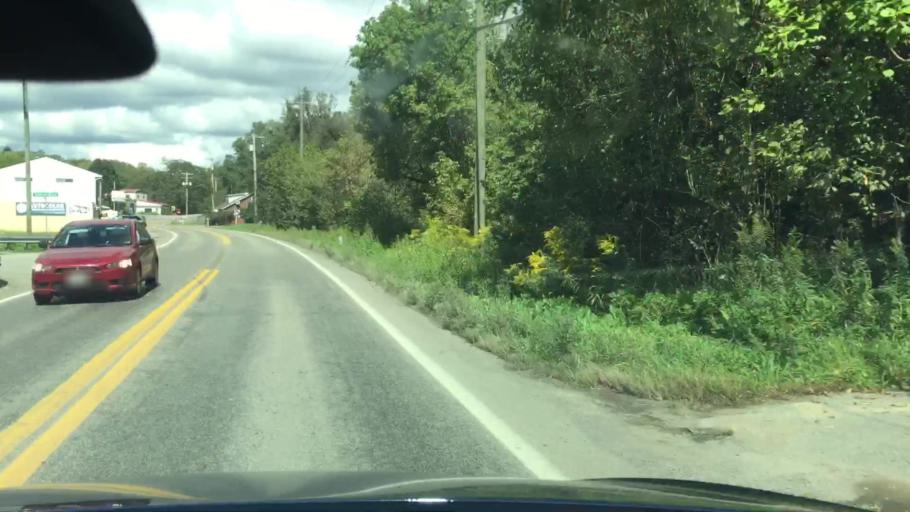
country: US
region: Pennsylvania
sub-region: Allegheny County
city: Russellton
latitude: 40.6199
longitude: -79.8335
